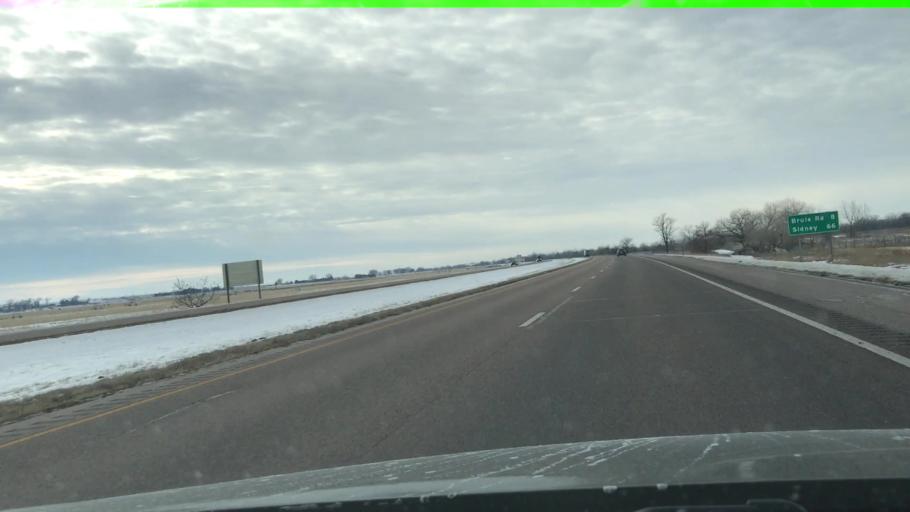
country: US
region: Nebraska
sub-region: Keith County
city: Ogallala
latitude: 41.1149
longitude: -101.7313
